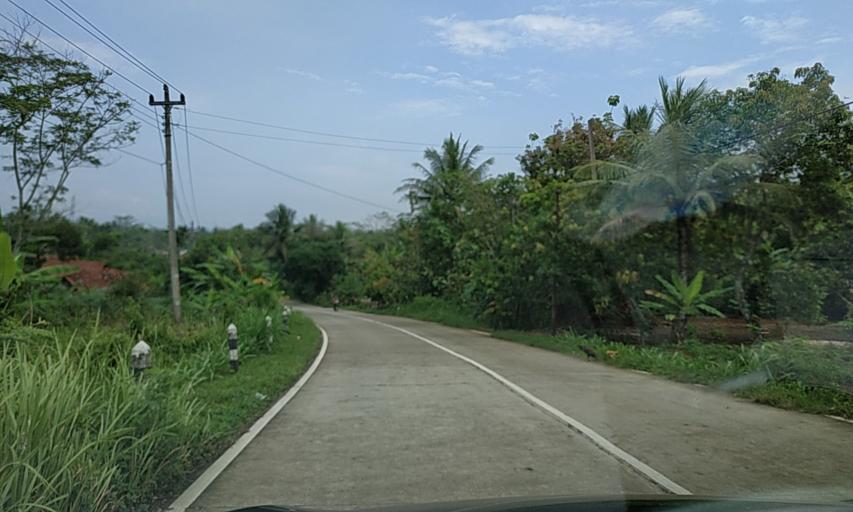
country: ID
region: Central Java
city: Ciloning
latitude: -7.4803
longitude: 108.8409
